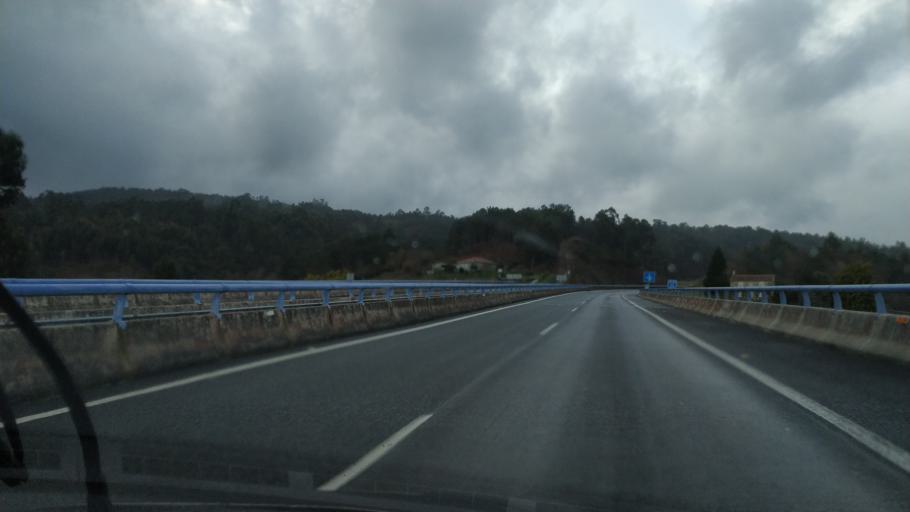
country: ES
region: Galicia
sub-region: Provincia de Pontevedra
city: Silleda
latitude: 42.7292
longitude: -8.3316
